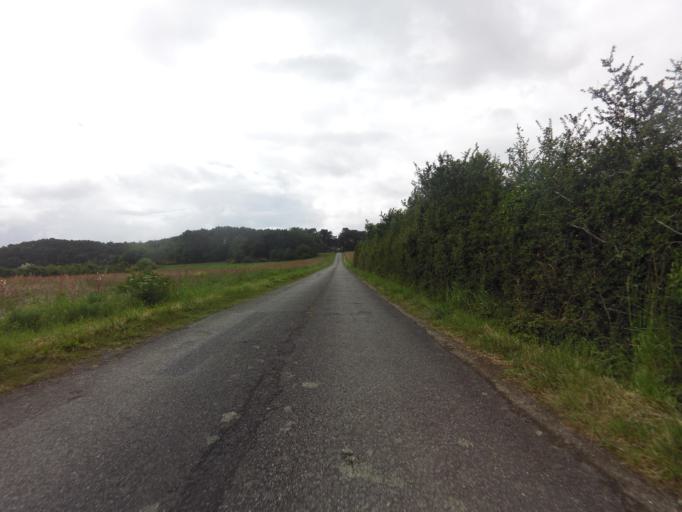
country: FR
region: Brittany
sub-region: Departement du Morbihan
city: Baden
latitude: 47.5983
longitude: -2.9367
